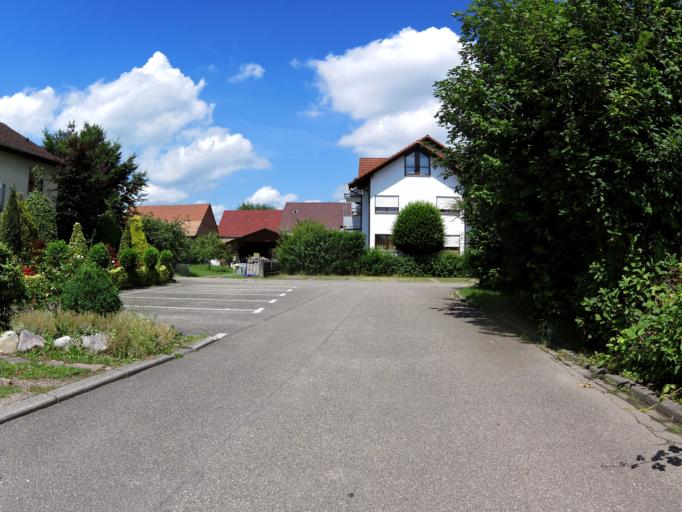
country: DE
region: Baden-Wuerttemberg
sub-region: Freiburg Region
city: Kippenheim
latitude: 48.3172
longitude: 7.8069
